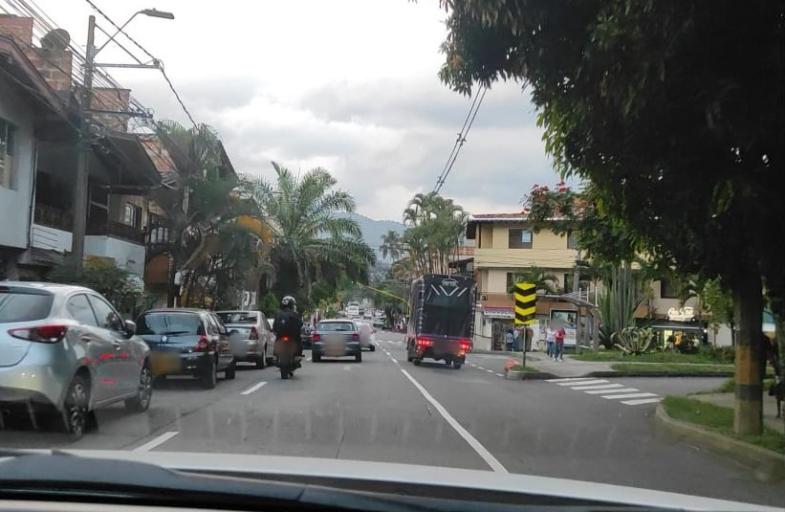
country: CO
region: Antioquia
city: Envigado
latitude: 6.1670
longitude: -75.5819
